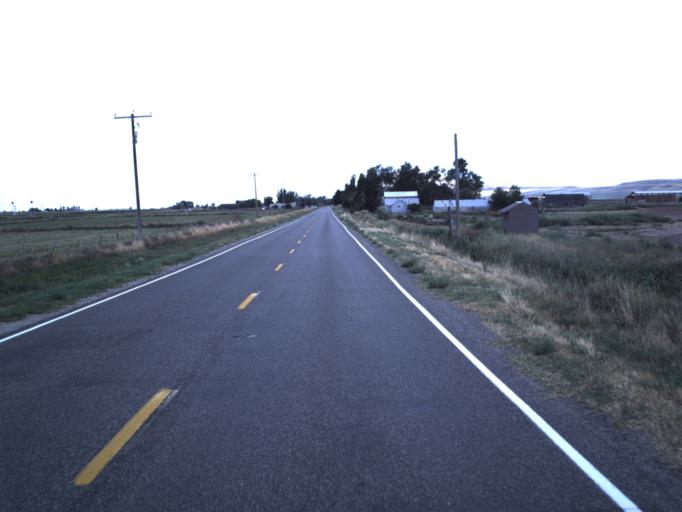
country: US
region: Utah
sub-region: Cache County
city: Lewiston
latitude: 41.9842
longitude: -111.9545
